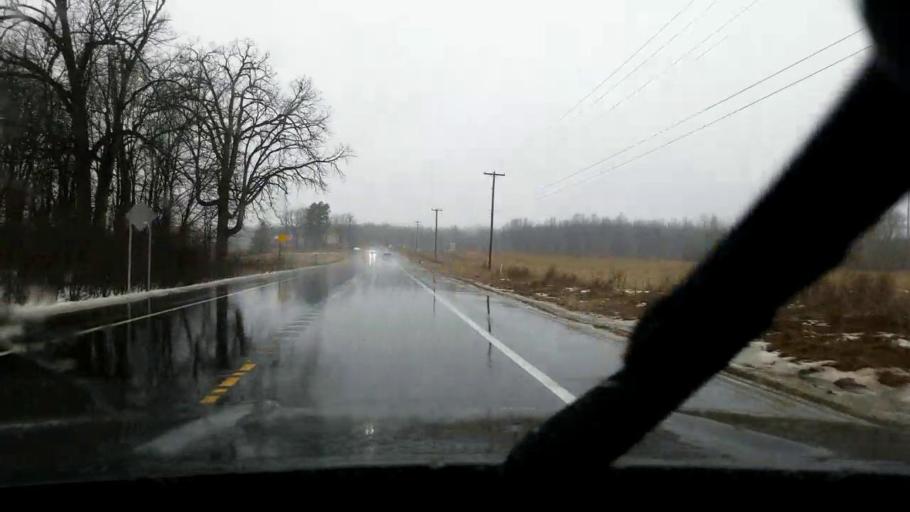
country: US
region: Michigan
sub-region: Jackson County
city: Napoleon
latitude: 42.1794
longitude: -84.2887
